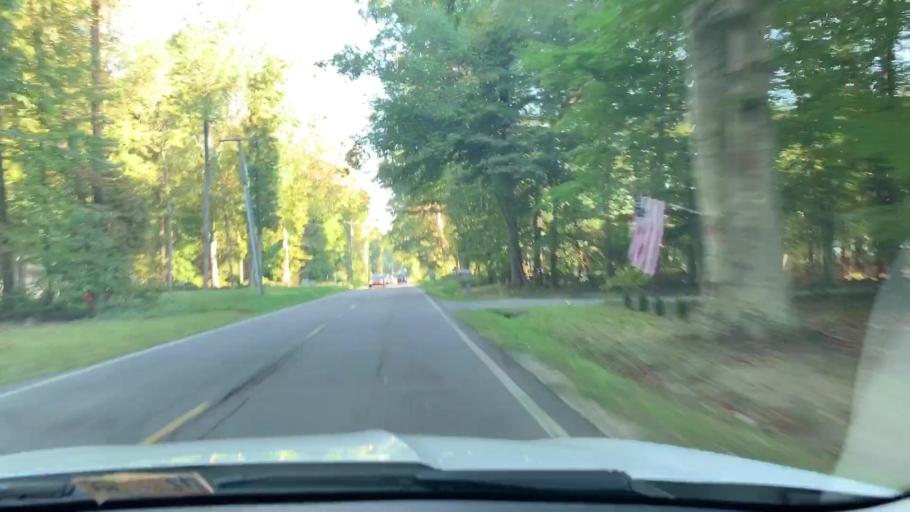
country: US
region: Virginia
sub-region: Gloucester County
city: Gloucester Courthouse
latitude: 37.4690
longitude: -76.4453
